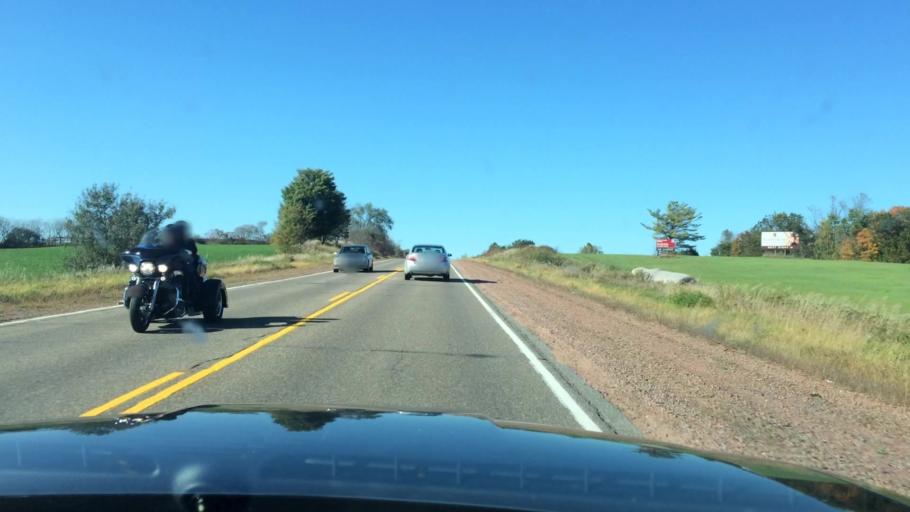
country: US
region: Wisconsin
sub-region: Marathon County
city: Wausau
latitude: 45.0037
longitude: -89.6700
